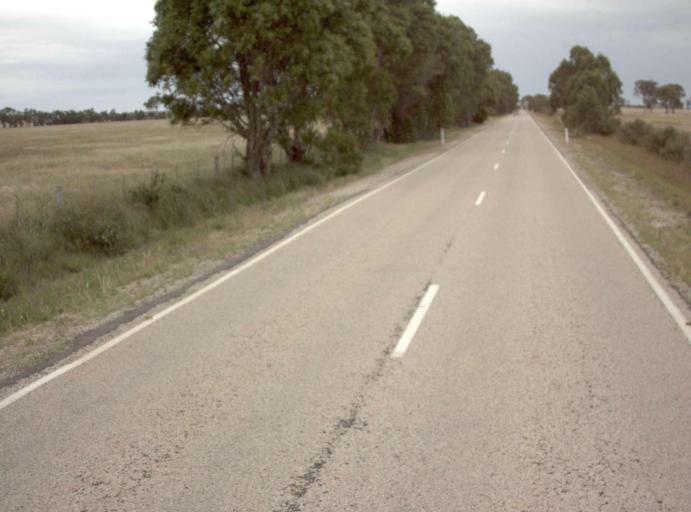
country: AU
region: Victoria
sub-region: East Gippsland
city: Bairnsdale
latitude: -37.8936
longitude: 147.5558
